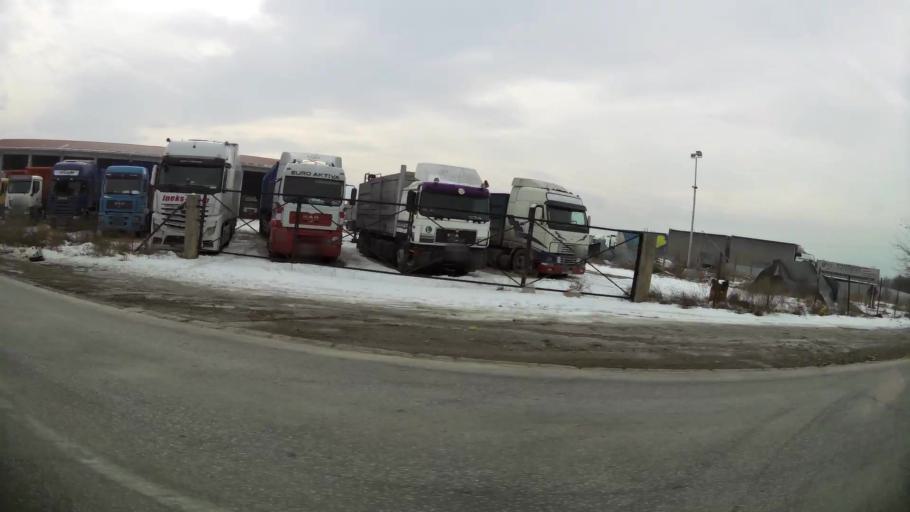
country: MK
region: Suto Orizari
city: Suto Orizare
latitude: 42.0434
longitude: 21.3906
